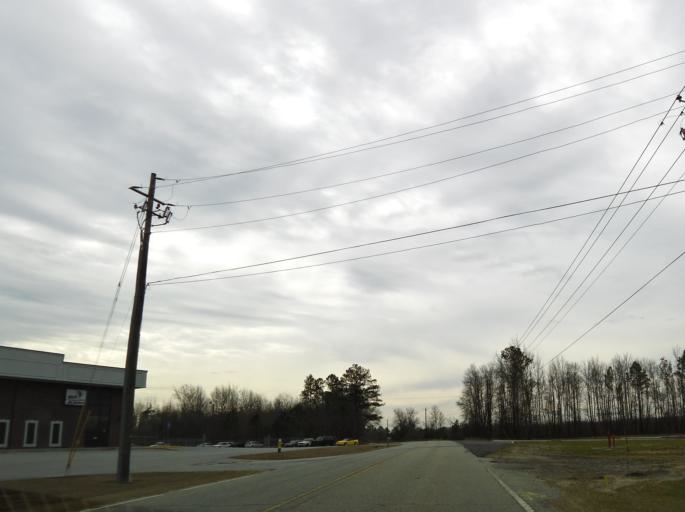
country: US
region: Georgia
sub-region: Houston County
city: Centerville
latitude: 32.6995
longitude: -83.6835
